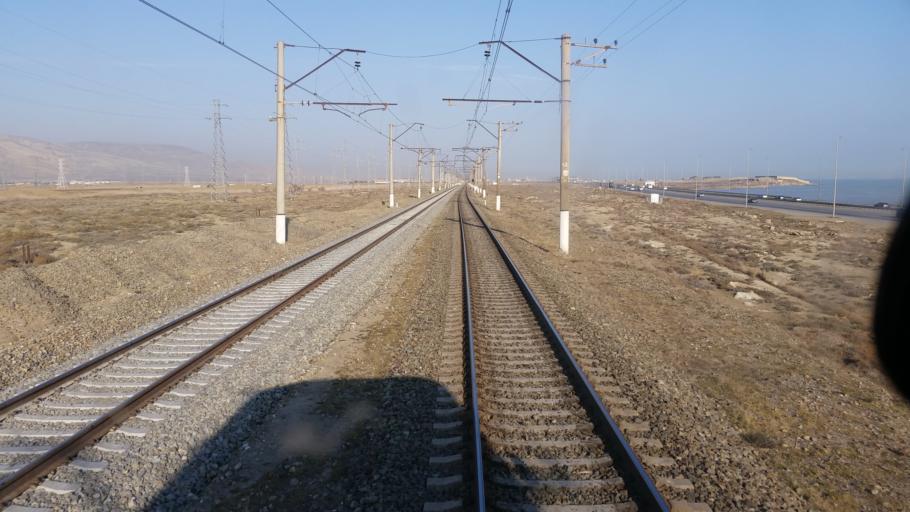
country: AZ
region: Baki
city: Qobustan
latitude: 40.1815
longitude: 49.4788
